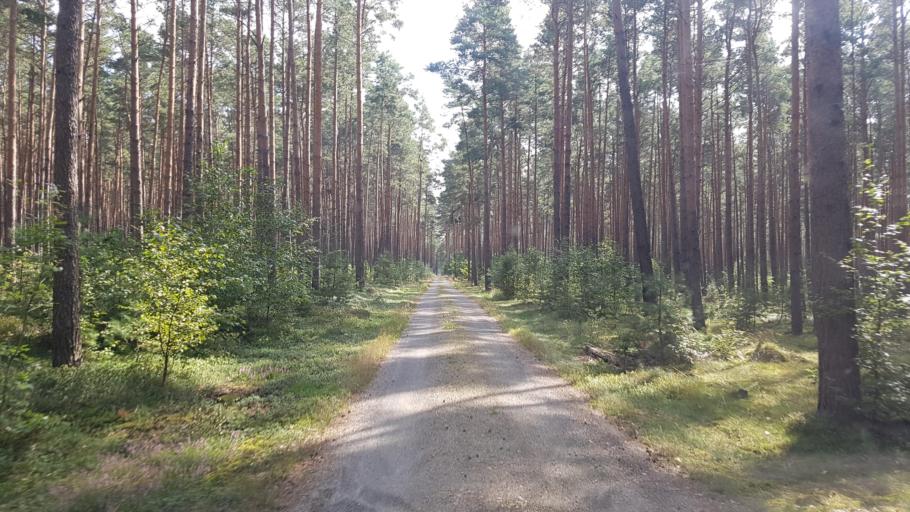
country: DE
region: Brandenburg
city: Hohenbucko
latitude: 51.7822
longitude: 13.5260
